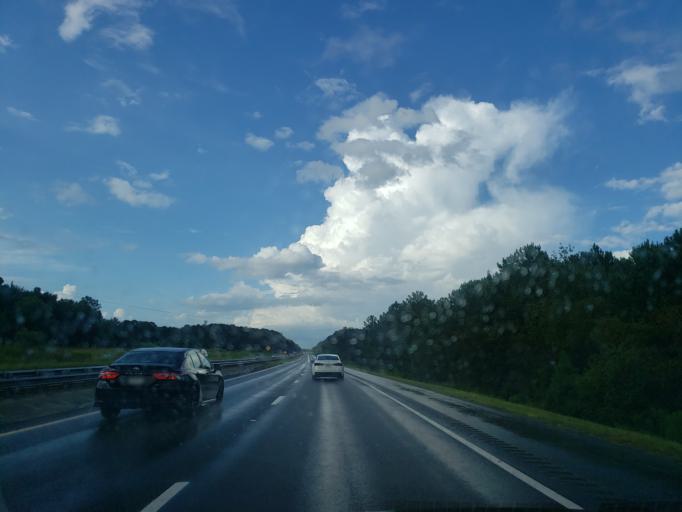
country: US
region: Georgia
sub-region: Chatham County
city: Georgetown
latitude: 32.0177
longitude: -81.1743
